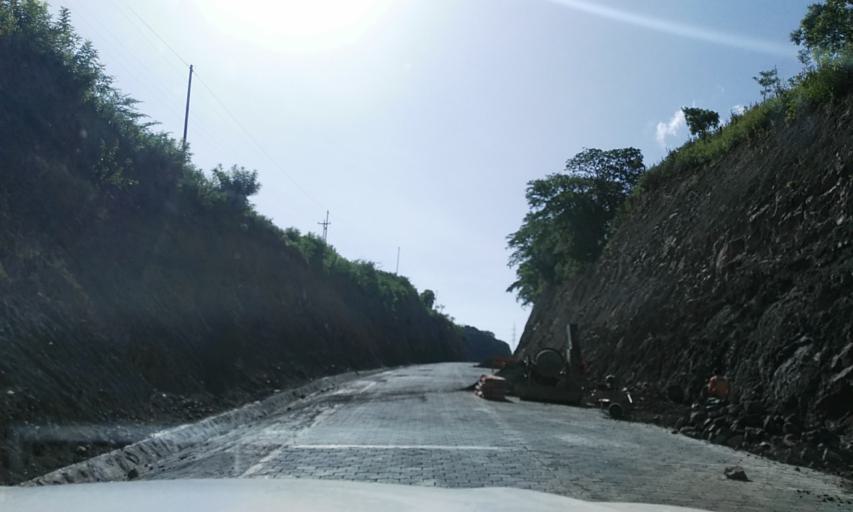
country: NI
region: Matagalpa
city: Terrabona
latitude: 12.7541
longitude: -85.9817
